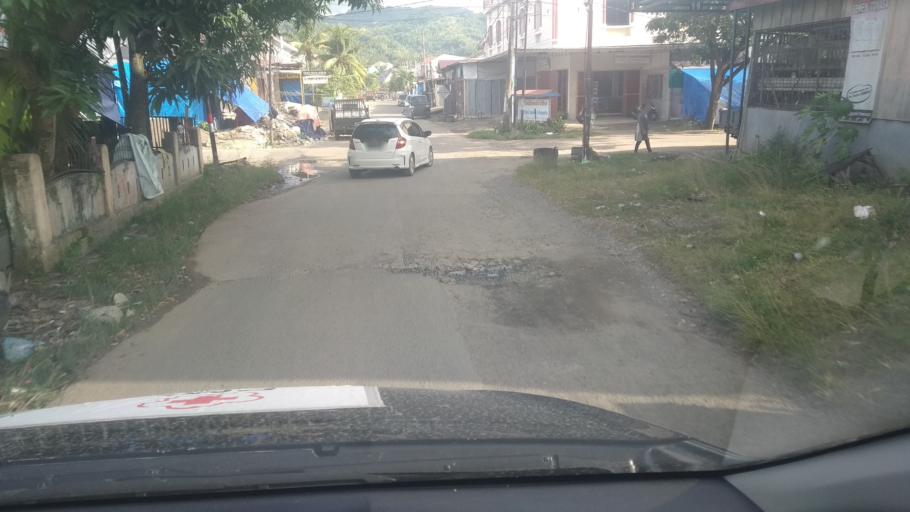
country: ID
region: Sulawesi Barat
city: Mamuju
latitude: -2.6778
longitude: 118.8851
